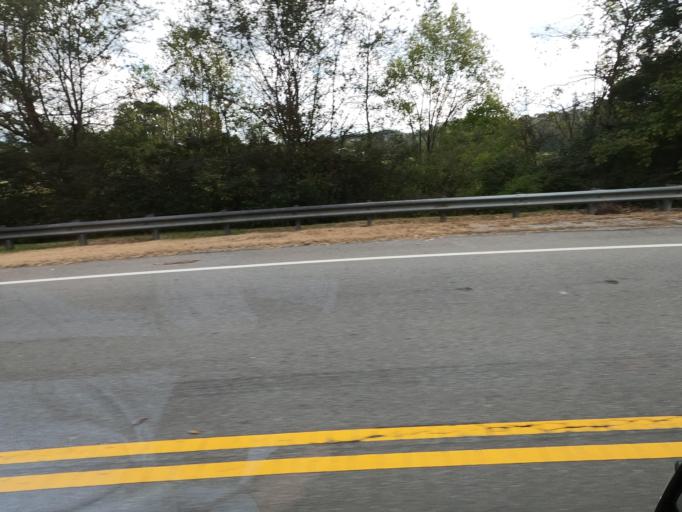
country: US
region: Tennessee
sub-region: Cheatham County
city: Pegram
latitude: 36.0872
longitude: -87.0244
